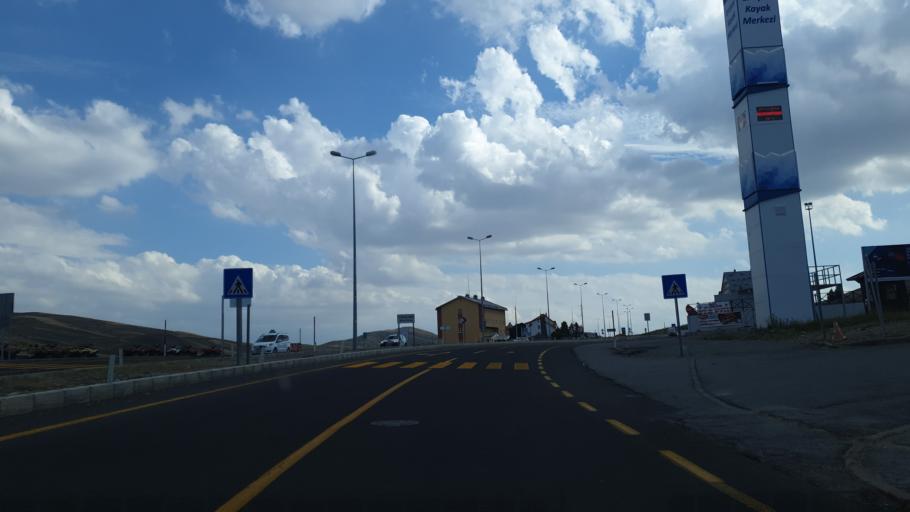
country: TR
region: Kayseri
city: Hacilar
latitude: 38.5405
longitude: 35.5279
